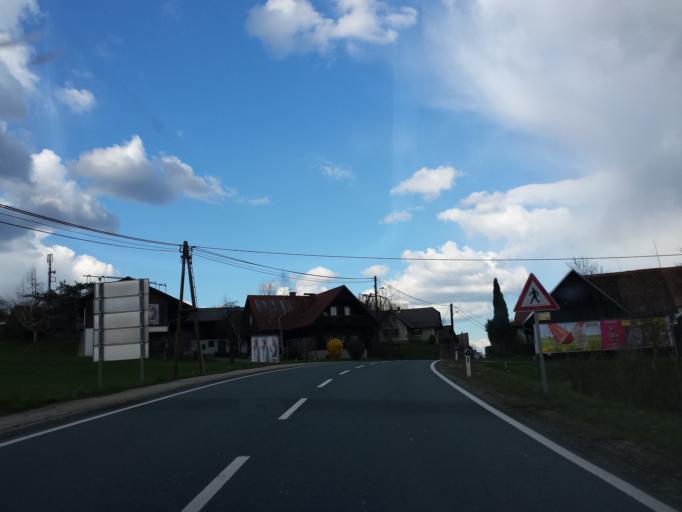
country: AT
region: Styria
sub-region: Politischer Bezirk Deutschlandsberg
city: Sankt Stefan ob Stainz
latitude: 46.9269
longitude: 15.2914
